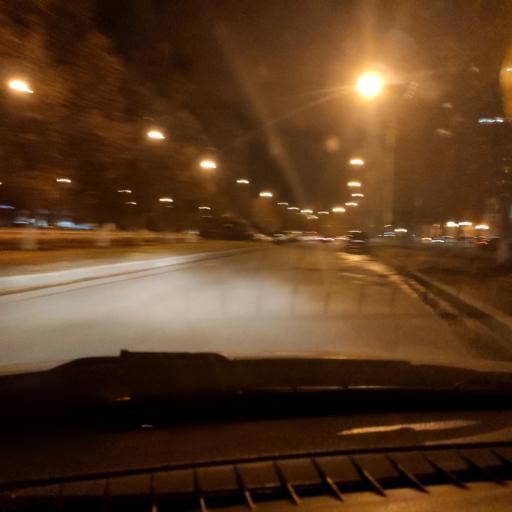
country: RU
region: Samara
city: Tol'yatti
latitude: 53.5173
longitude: 49.3028
